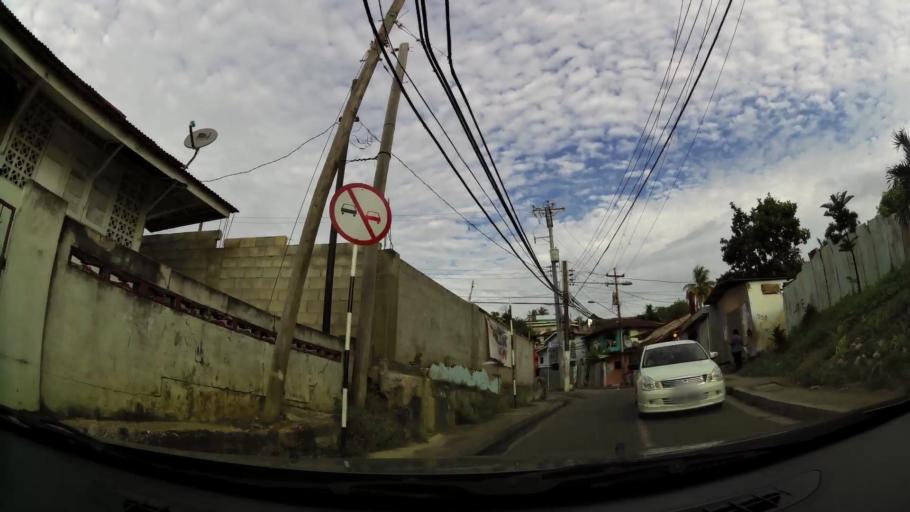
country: TT
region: San Juan/Laventille
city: Laventille
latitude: 10.6548
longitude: -61.5043
